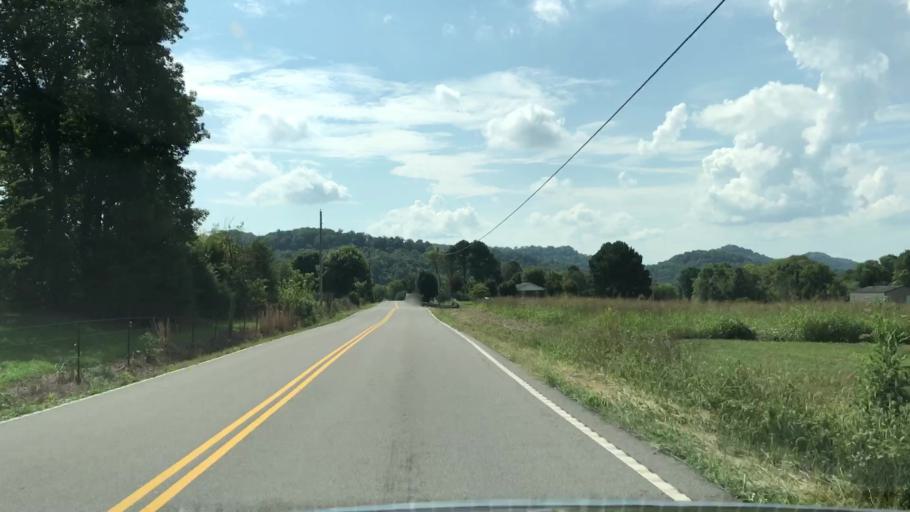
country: US
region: Tennessee
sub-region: Trousdale County
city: Hartsville
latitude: 36.4699
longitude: -86.1777
